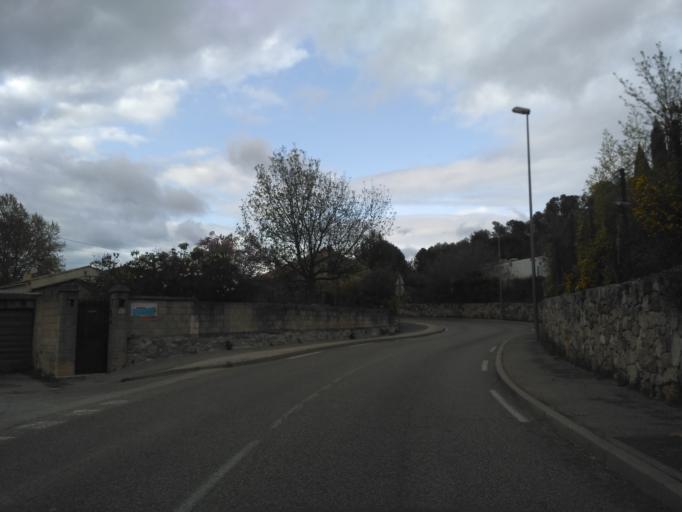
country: FR
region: Provence-Alpes-Cote d'Azur
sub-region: Departement du Var
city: Barjols
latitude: 43.5615
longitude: 6.0085
